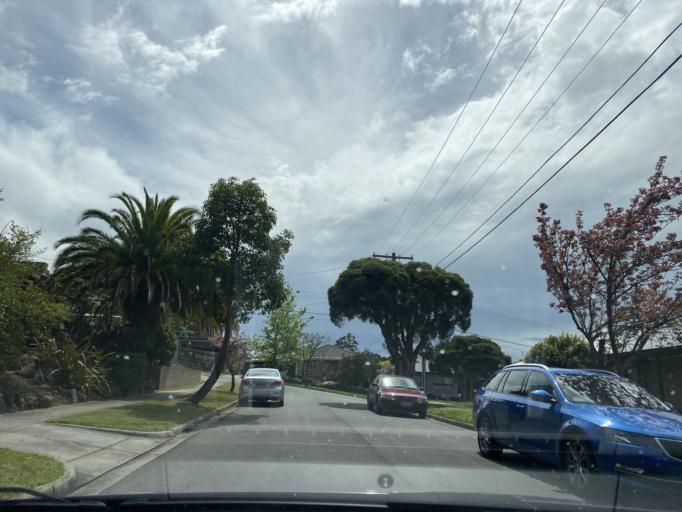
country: AU
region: Victoria
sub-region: Manningham
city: Templestowe Lower
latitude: -37.7697
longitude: 145.1208
